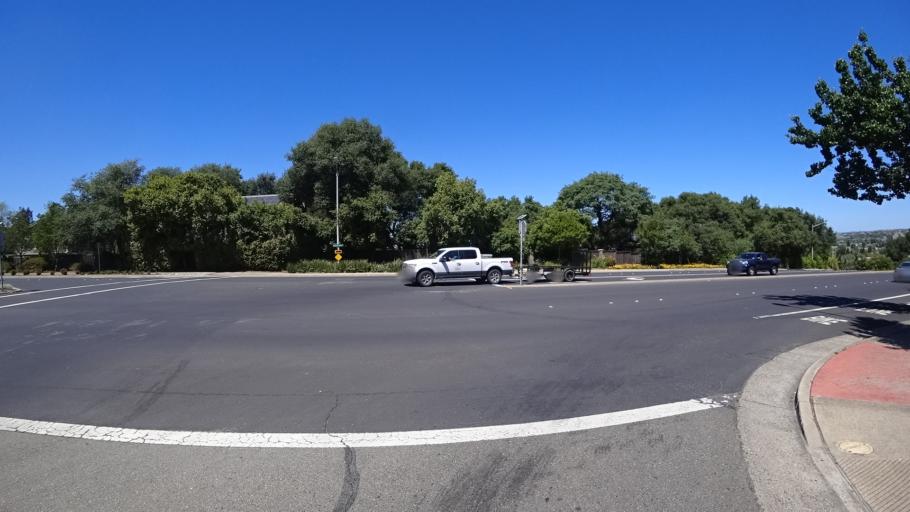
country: US
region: California
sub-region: Placer County
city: Rocklin
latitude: 38.8072
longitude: -121.2558
